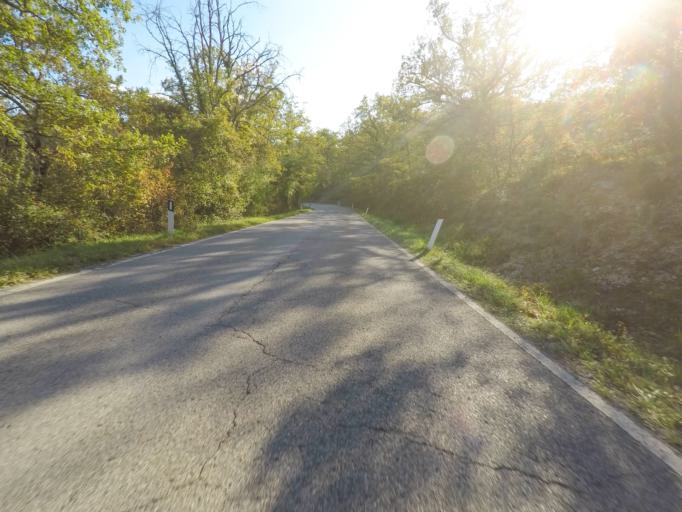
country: IT
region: Tuscany
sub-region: Provincia di Siena
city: Radda in Chianti
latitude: 43.4729
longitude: 11.3742
